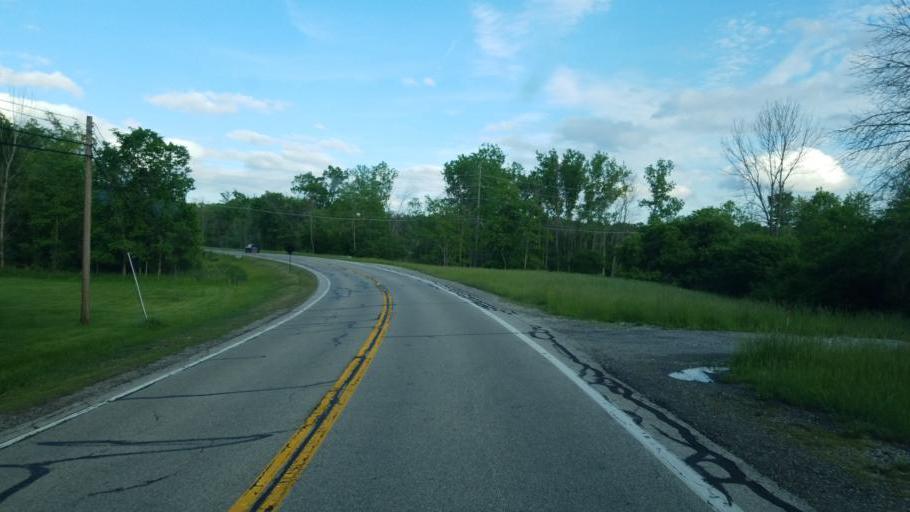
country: US
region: Ohio
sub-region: Summit County
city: Hudson
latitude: 41.2564
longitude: -81.4465
